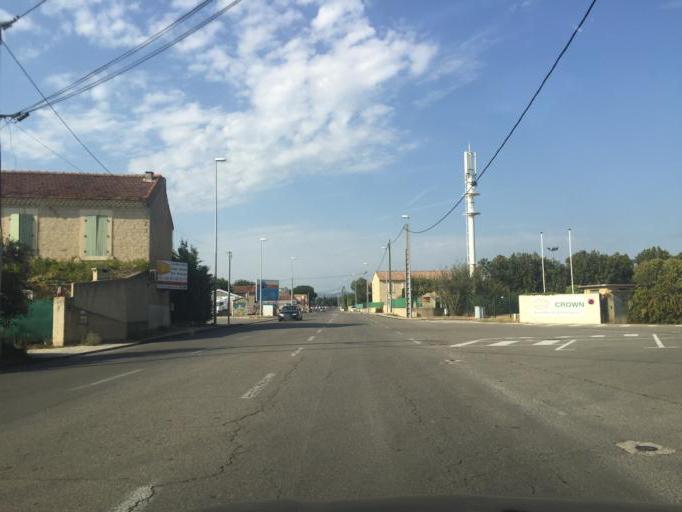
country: FR
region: Provence-Alpes-Cote d'Azur
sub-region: Departement du Vaucluse
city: Carpentras
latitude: 44.0381
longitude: 5.0404
